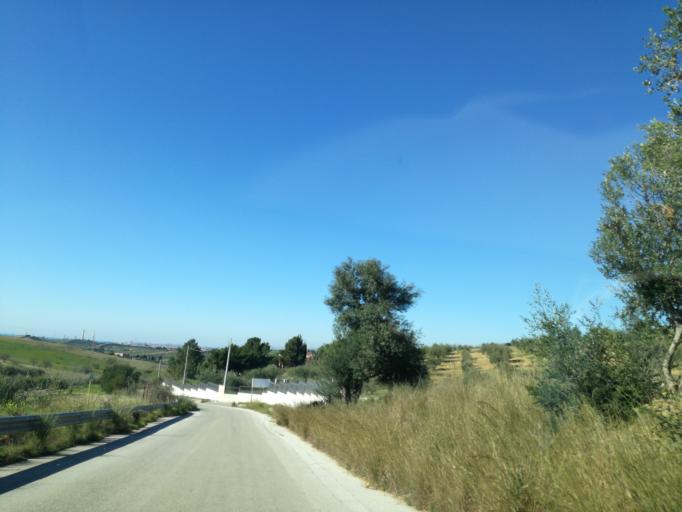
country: IT
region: Sicily
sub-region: Provincia di Caltanissetta
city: Niscemi
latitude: 37.0609
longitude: 14.3470
